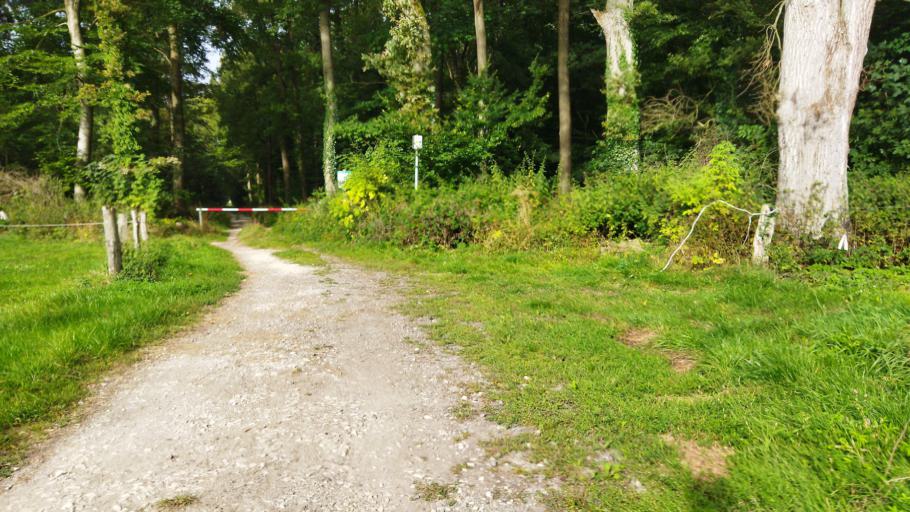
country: DE
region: Lower Saxony
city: Bad Rothenfelde
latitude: 52.0821
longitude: 8.1614
